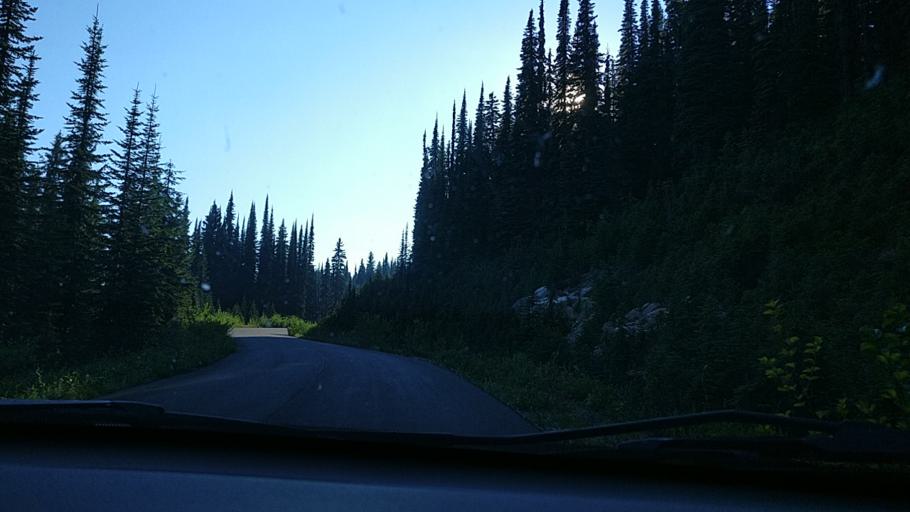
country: CA
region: British Columbia
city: Revelstoke
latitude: 51.0267
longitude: -118.1573
